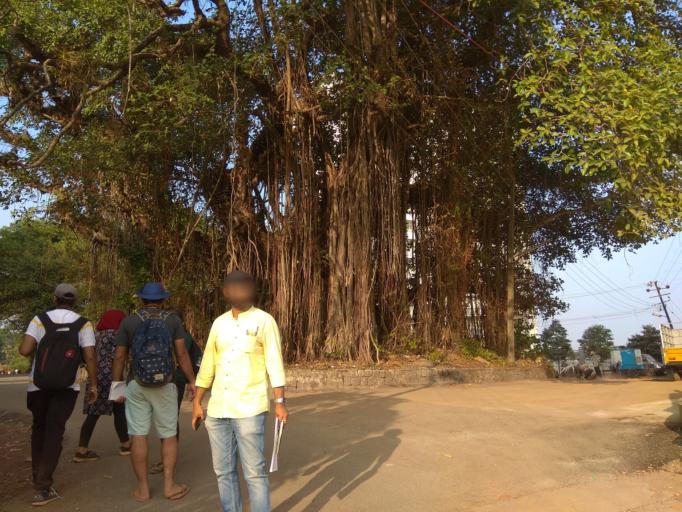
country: IN
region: Karnataka
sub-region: Dakshina Kannada
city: Ullal
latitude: 12.8434
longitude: 74.8530
